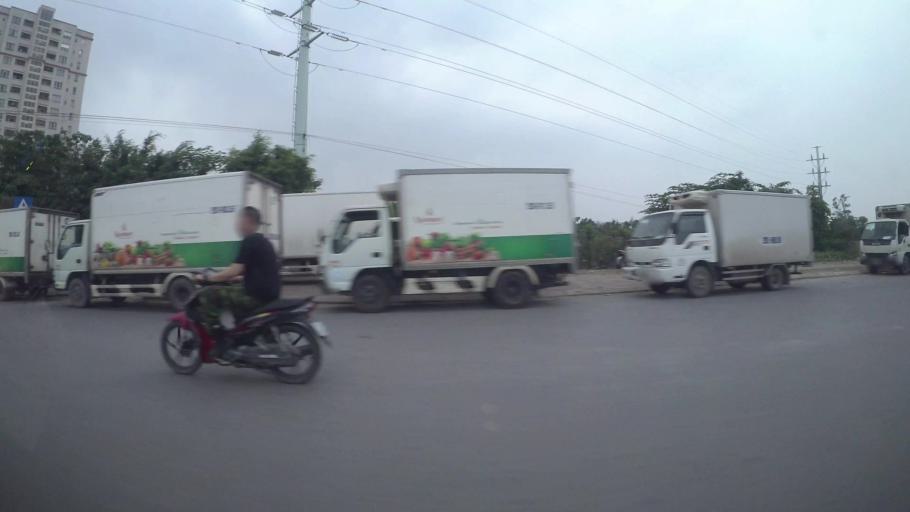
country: VN
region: Ha Noi
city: Trau Quy
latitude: 21.0410
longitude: 105.9132
